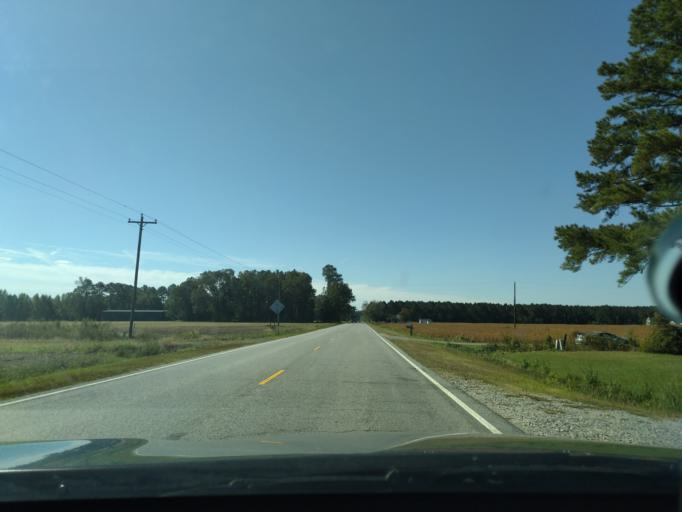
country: US
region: North Carolina
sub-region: Washington County
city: Plymouth
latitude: 35.6872
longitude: -76.7757
